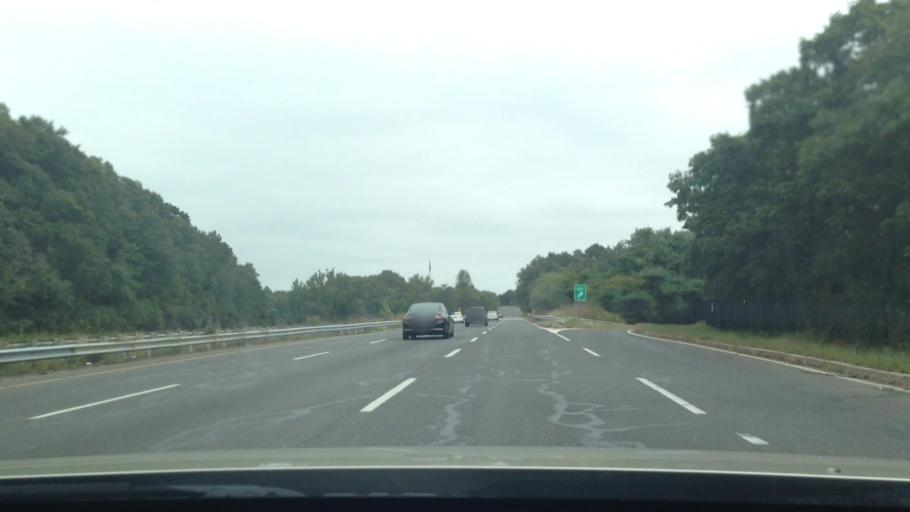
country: US
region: New York
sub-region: Suffolk County
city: Farmingville
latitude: 40.8412
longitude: -73.0194
